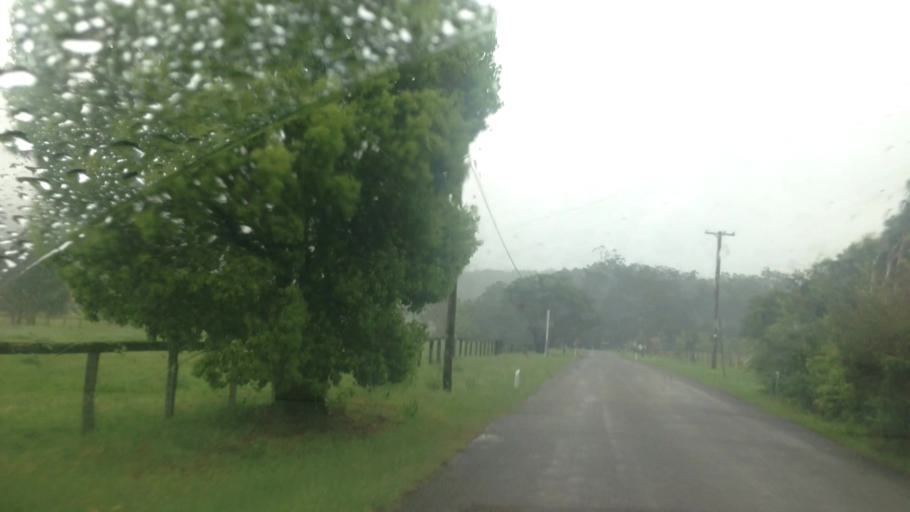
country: AU
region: New South Wales
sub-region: Wyong Shire
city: Little Jilliby
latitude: -33.1901
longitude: 151.3581
